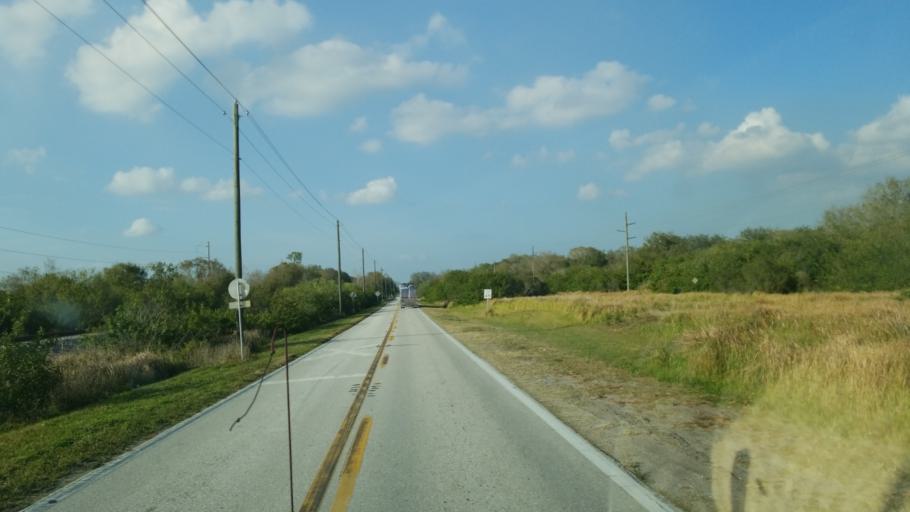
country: US
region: Florida
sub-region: Hardee County
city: Bowling Green
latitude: 27.6885
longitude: -81.9560
